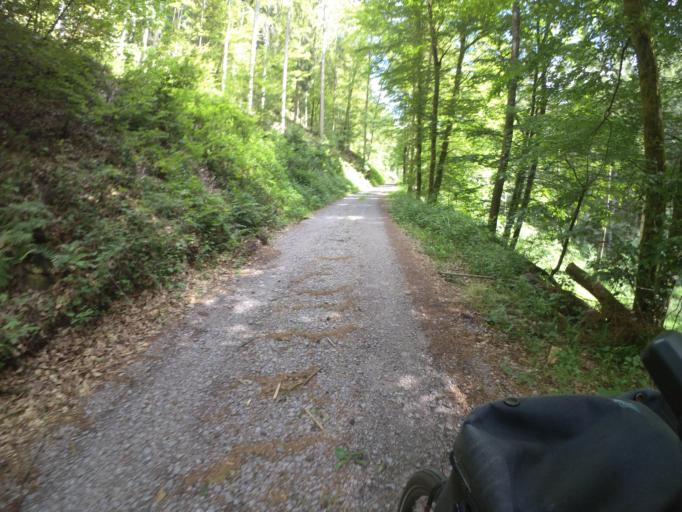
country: DE
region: Rheinland-Pfalz
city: Fischbach
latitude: 49.1233
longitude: 7.6941
